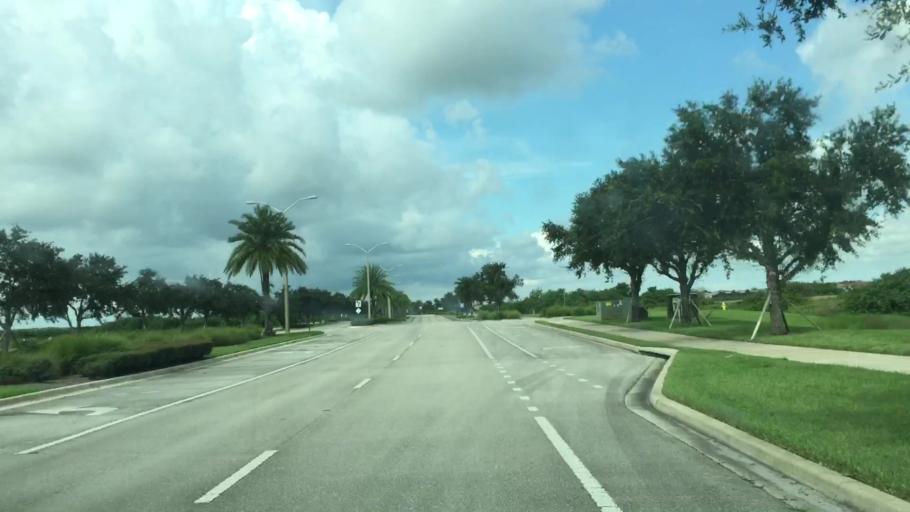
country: US
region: Florida
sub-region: Collier County
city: Immokalee
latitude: 26.3392
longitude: -81.4192
